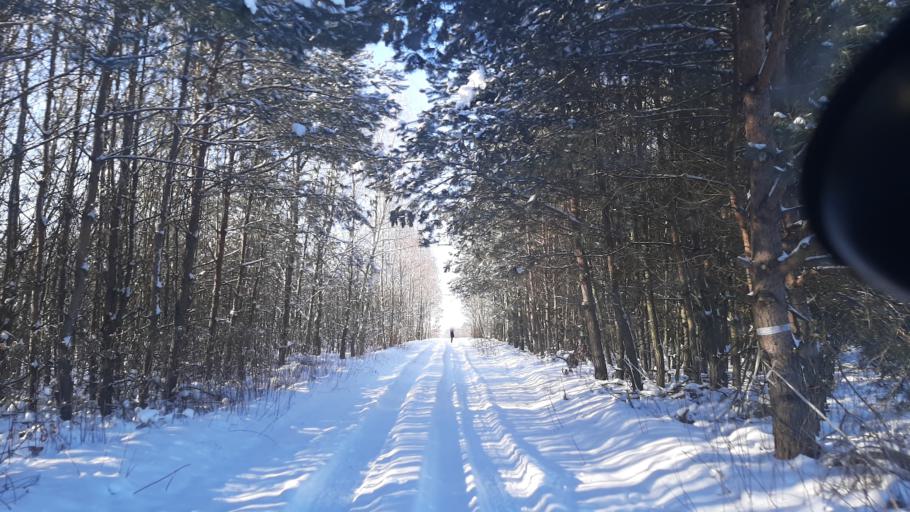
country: PL
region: Lublin Voivodeship
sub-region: Powiat lubelski
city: Jastkow
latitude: 51.3764
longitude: 22.4385
